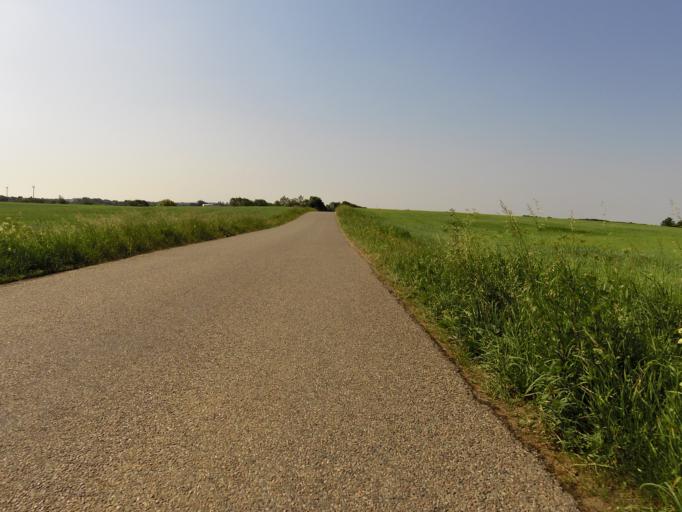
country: DK
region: Central Jutland
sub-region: Holstebro Kommune
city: Vinderup
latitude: 56.4812
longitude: 8.8306
